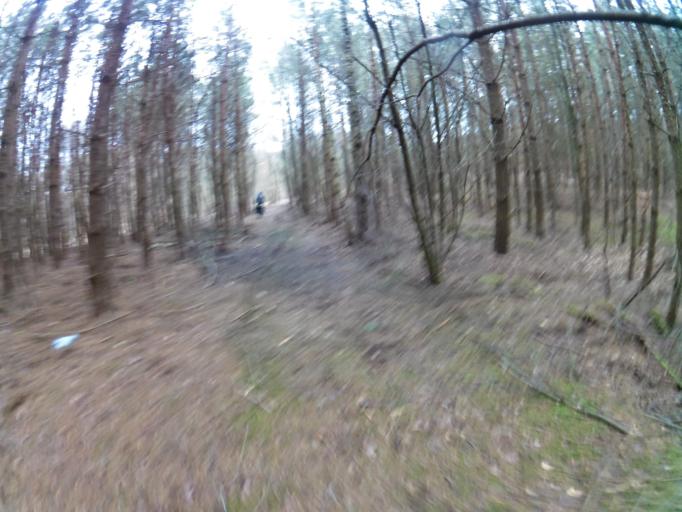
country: PL
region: West Pomeranian Voivodeship
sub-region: Powiat mysliborski
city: Debno
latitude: 52.7230
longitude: 14.7371
